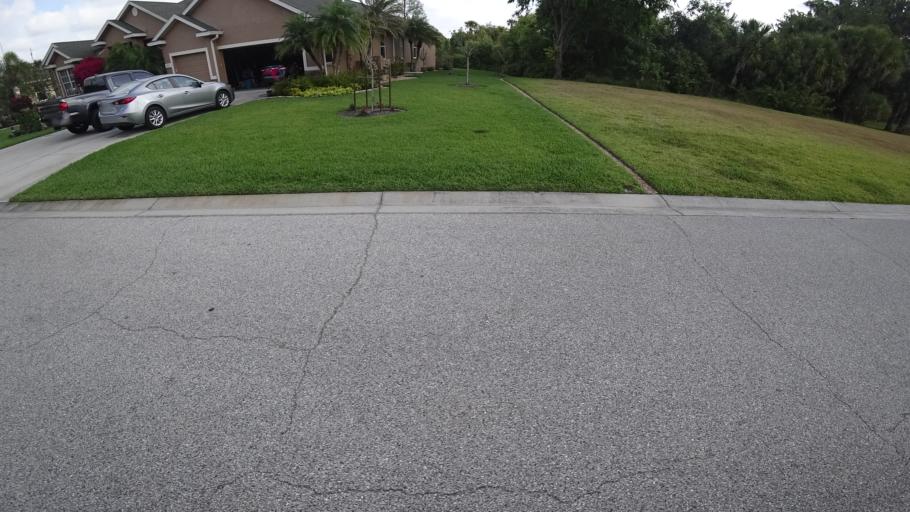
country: US
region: Florida
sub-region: Manatee County
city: Ellenton
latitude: 27.5664
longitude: -82.4731
